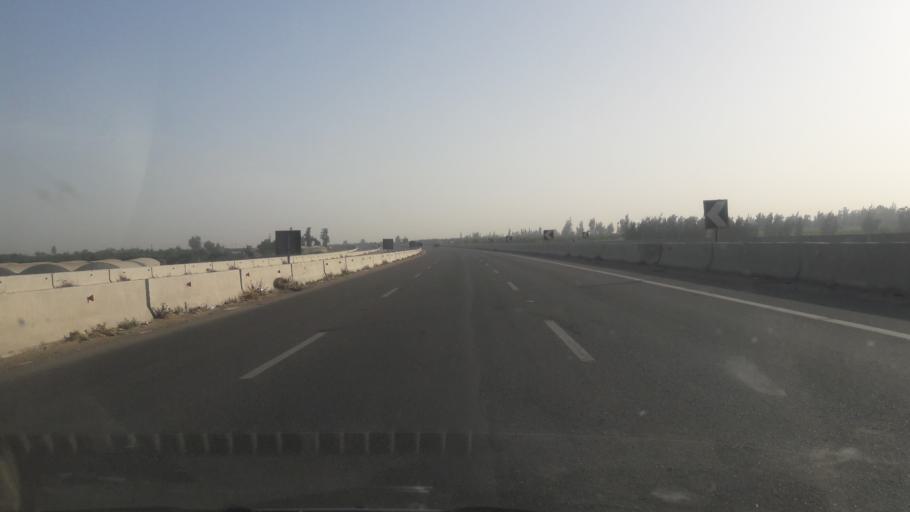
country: EG
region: Al Isma'iliyah
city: Ismailia
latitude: 30.6375
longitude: 32.0901
